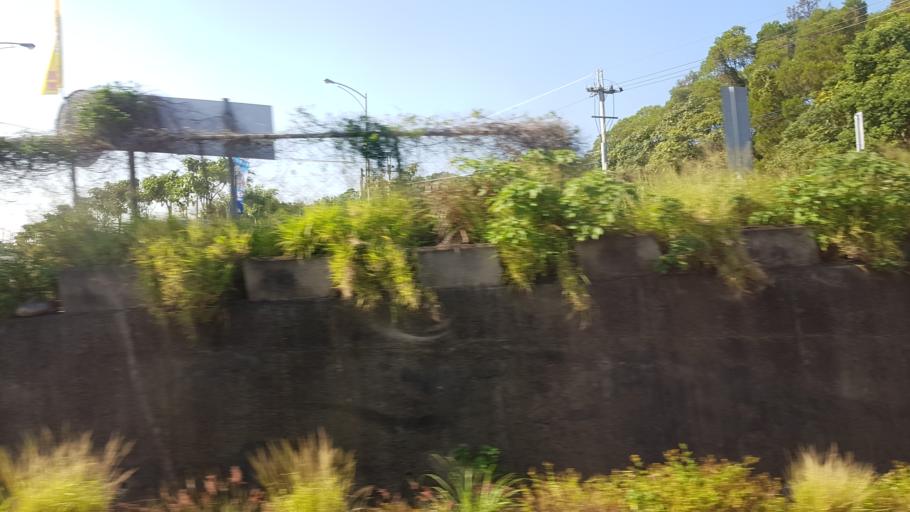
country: TW
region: Taiwan
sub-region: Miaoli
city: Miaoli
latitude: 24.6127
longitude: 120.8348
